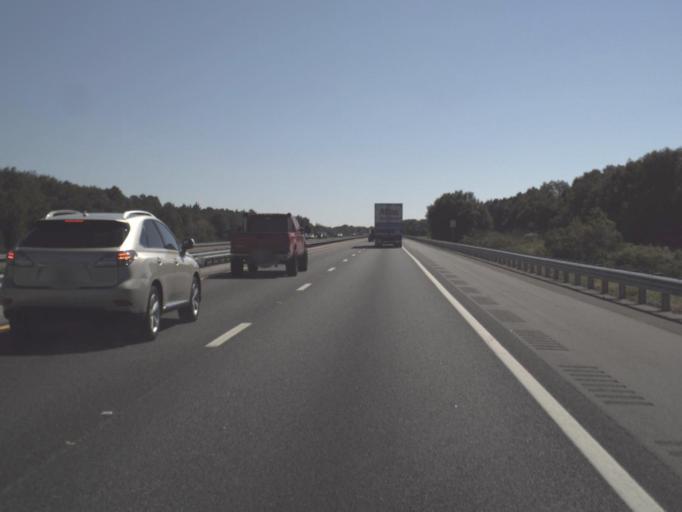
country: US
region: Florida
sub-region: Lake County
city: Hawthorne
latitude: 28.7475
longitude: -81.9306
